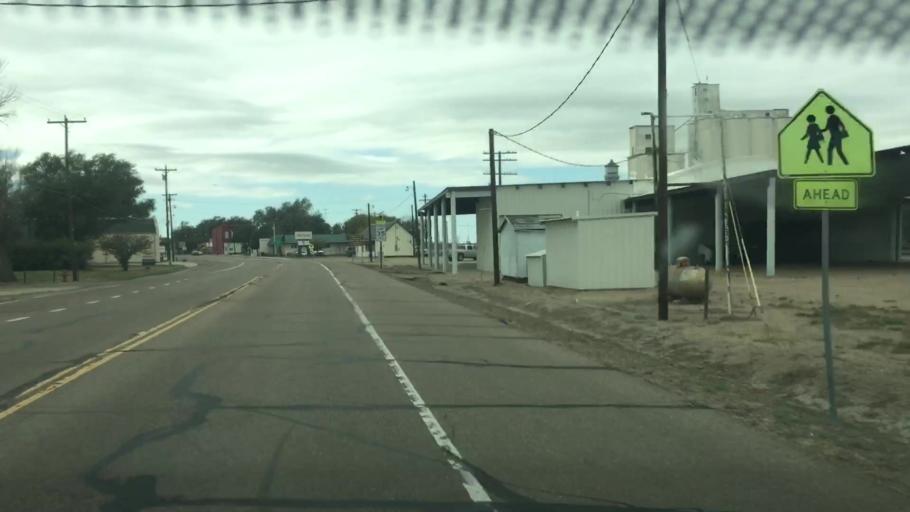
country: US
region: Colorado
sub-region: Prowers County
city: Lamar
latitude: 38.0625
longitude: -102.3071
